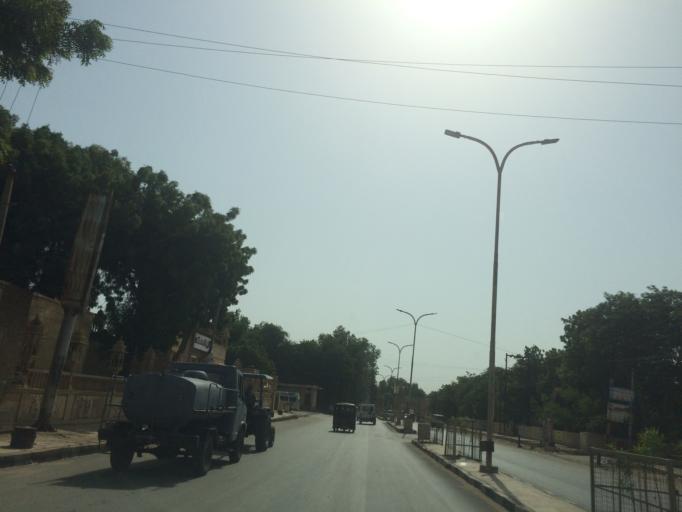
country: IN
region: Rajasthan
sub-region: Jaisalmer
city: Jaisalmer
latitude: 26.9090
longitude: 70.9136
